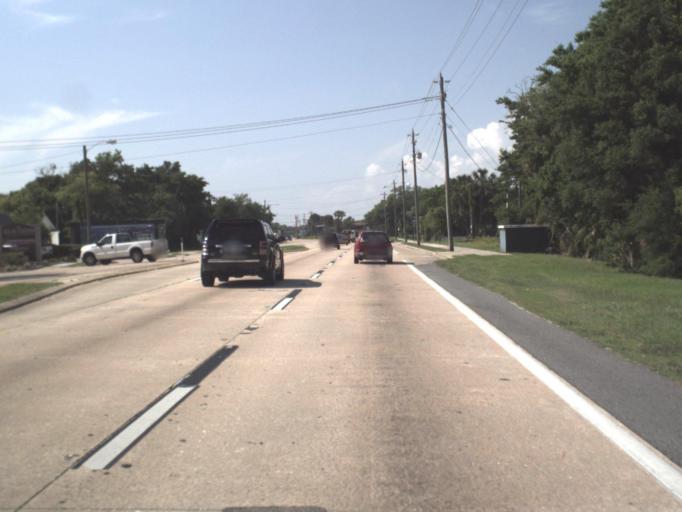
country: US
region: Florida
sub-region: Saint Johns County
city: Saint Augustine
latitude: 29.9073
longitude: -81.3216
